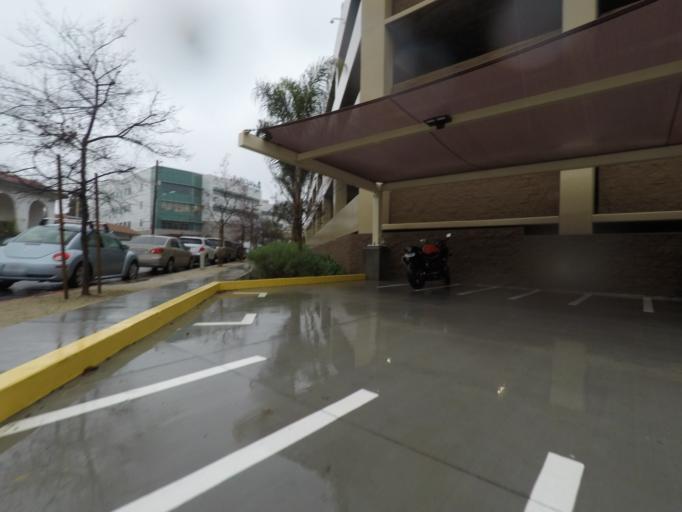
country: US
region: California
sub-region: San Diego County
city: San Diego
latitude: 32.7973
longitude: -117.1537
